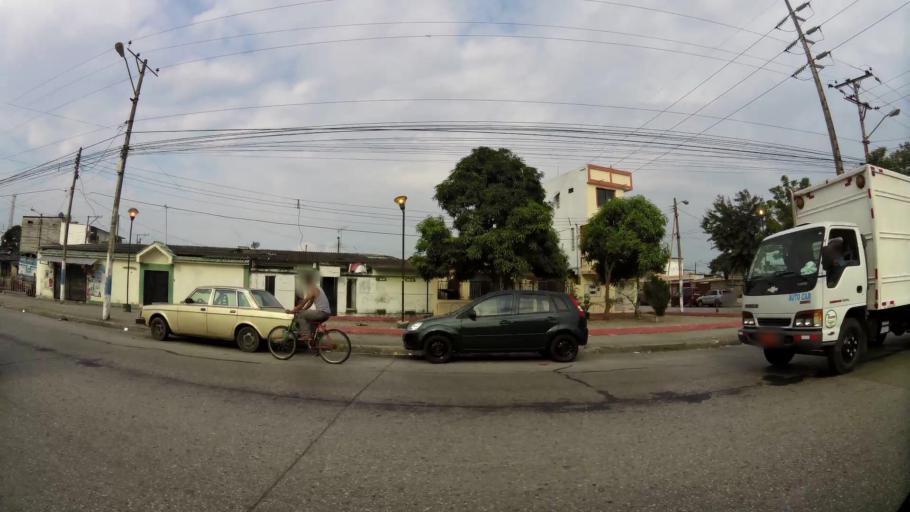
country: EC
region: Guayas
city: Guayaquil
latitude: -2.2496
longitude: -79.9032
